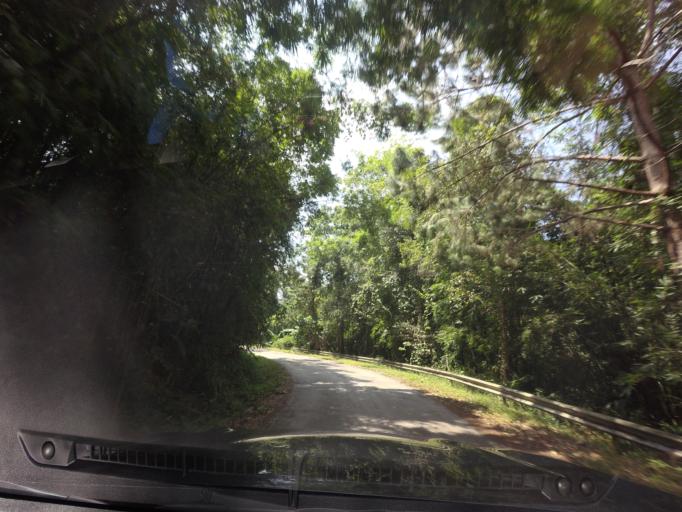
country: TH
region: Loei
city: Na Haeo
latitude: 17.4804
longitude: 100.9392
